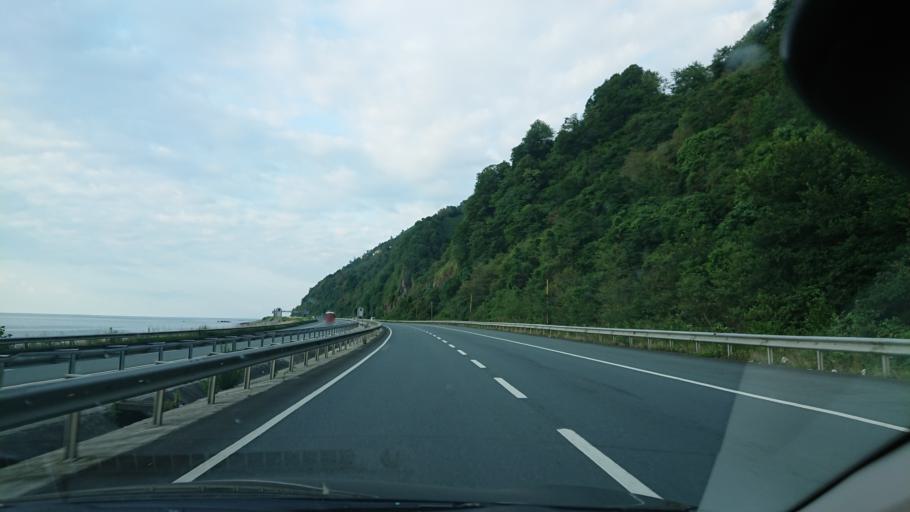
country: TR
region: Rize
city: Cayeli
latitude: 41.1384
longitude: 40.7724
